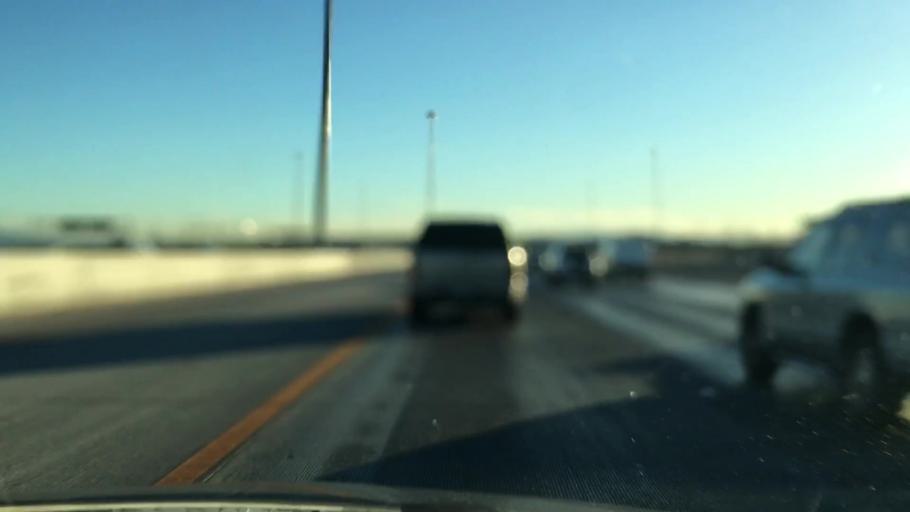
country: US
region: Nevada
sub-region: Clark County
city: Enterprise
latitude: 36.0668
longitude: -115.2289
